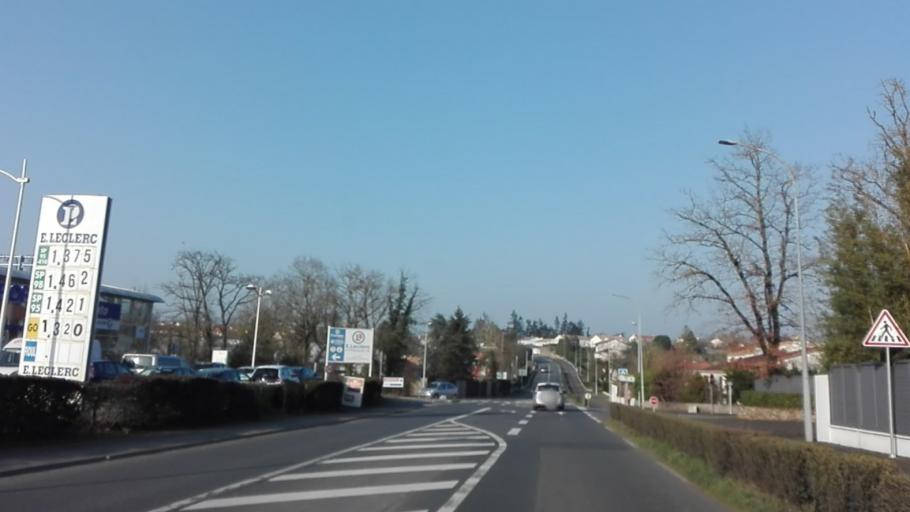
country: FR
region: Pays de la Loire
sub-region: Departement de la Vendee
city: Montaigu
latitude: 46.9749
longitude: -1.3042
